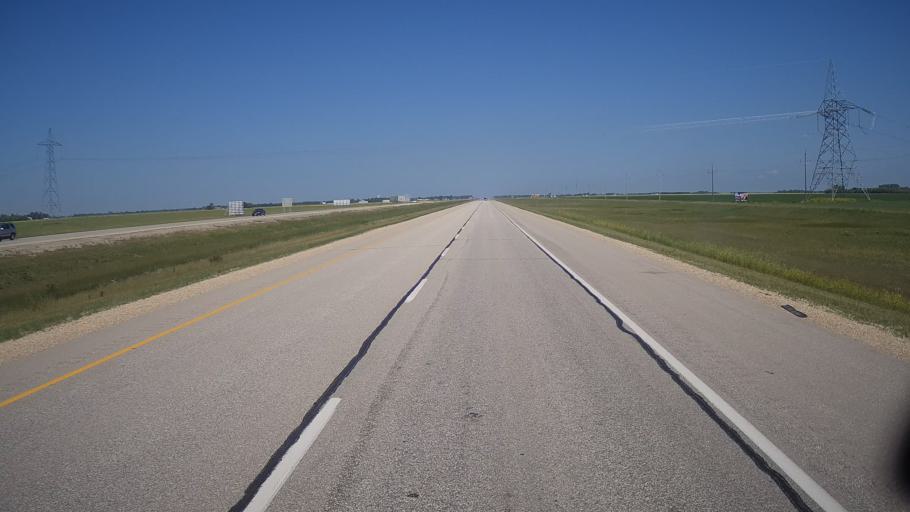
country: CA
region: Manitoba
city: Steinbach
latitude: 49.7115
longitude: -96.6718
